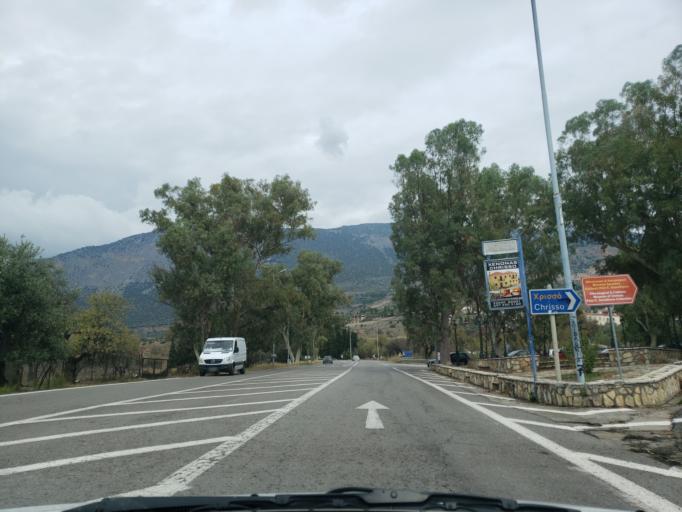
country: GR
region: Central Greece
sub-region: Nomos Fokidos
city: Delphi
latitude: 38.4731
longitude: 22.4625
